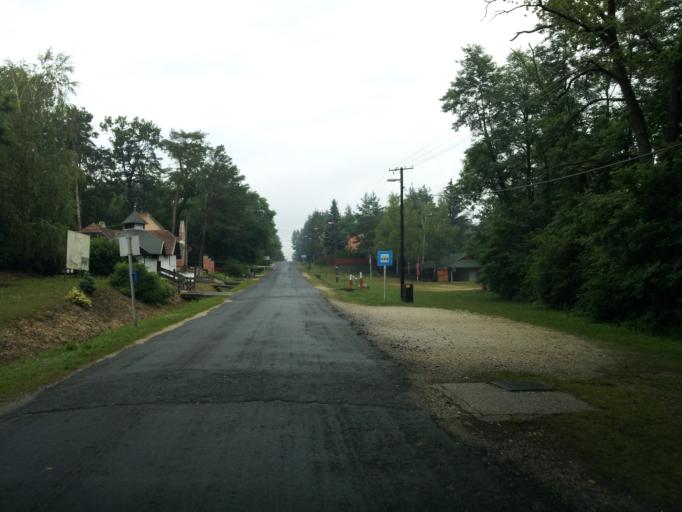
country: HU
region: Zala
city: Zalalovo
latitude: 46.8761
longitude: 16.5502
